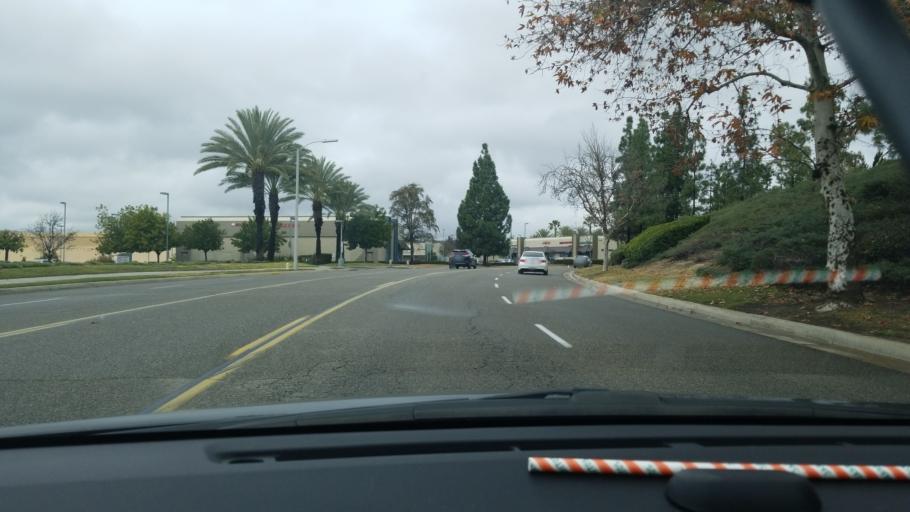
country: US
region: California
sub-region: Riverside County
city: Murrieta Hot Springs
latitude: 33.5585
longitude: -117.1782
